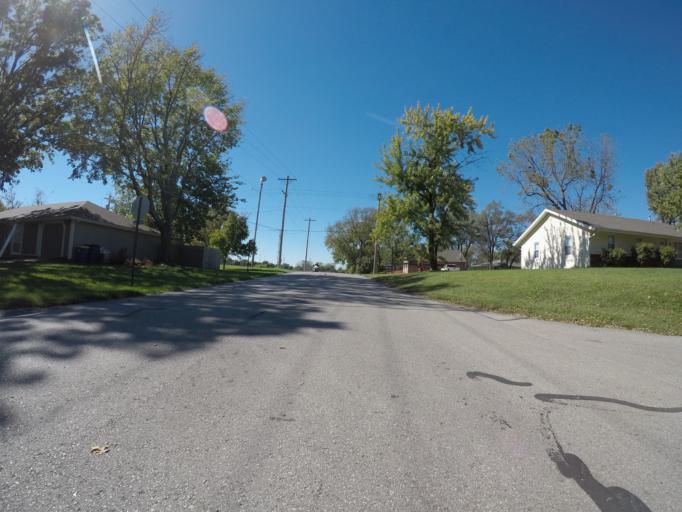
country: US
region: Kansas
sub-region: Douglas County
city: Eudora
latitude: 38.9389
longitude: -95.1067
